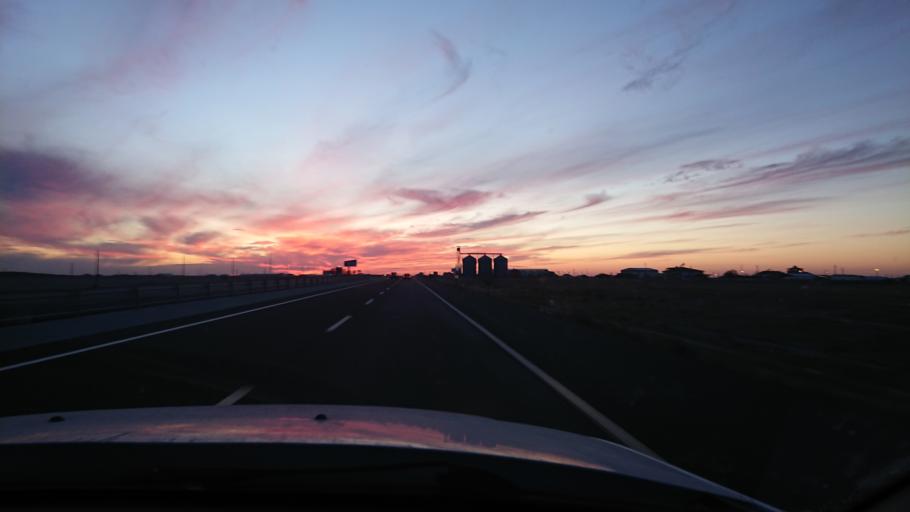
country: TR
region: Aksaray
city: Yesilova
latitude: 38.3294
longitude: 33.9010
